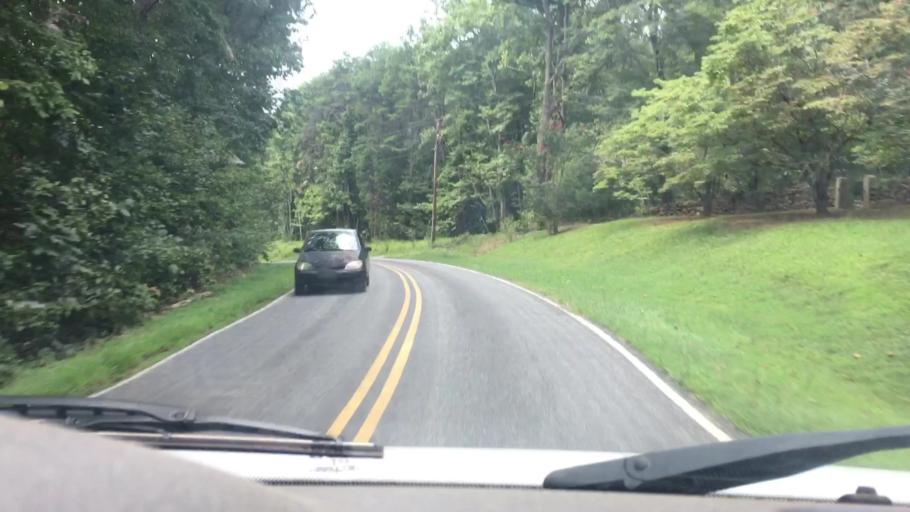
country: US
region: North Carolina
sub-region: Iredell County
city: Mooresville
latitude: 35.6616
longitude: -80.8067
